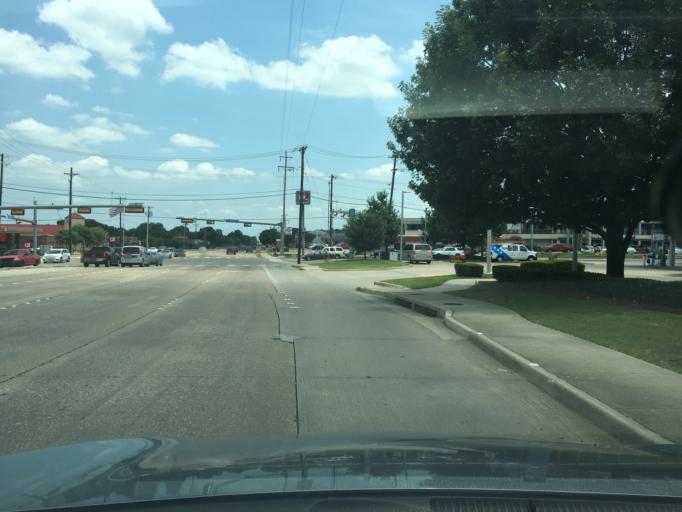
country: US
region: Texas
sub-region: Dallas County
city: Richardson
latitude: 32.9604
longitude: -96.6836
